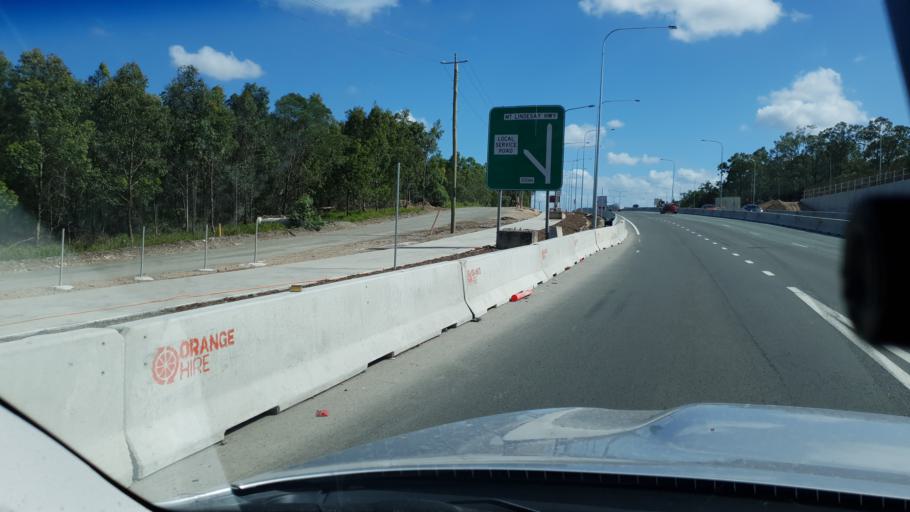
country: AU
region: Queensland
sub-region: Brisbane
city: Sunnybank Hills
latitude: -27.6490
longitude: 153.0412
